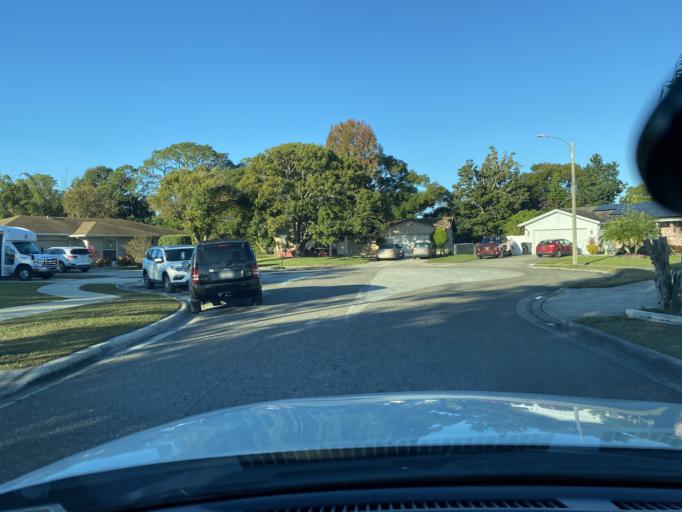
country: US
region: Florida
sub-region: Orange County
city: Azalea Park
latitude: 28.5275
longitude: -81.2973
